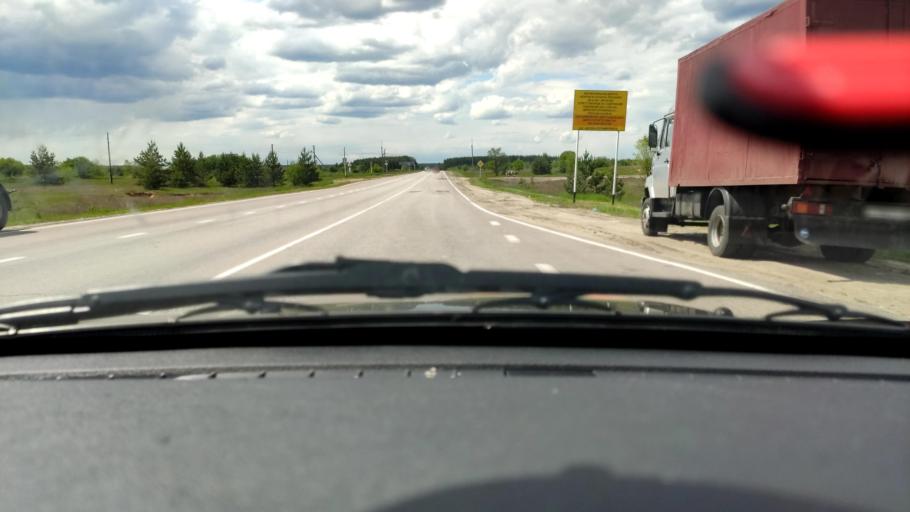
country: RU
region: Voronezj
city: Uryv-Pokrovka
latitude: 51.0493
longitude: 38.9828
